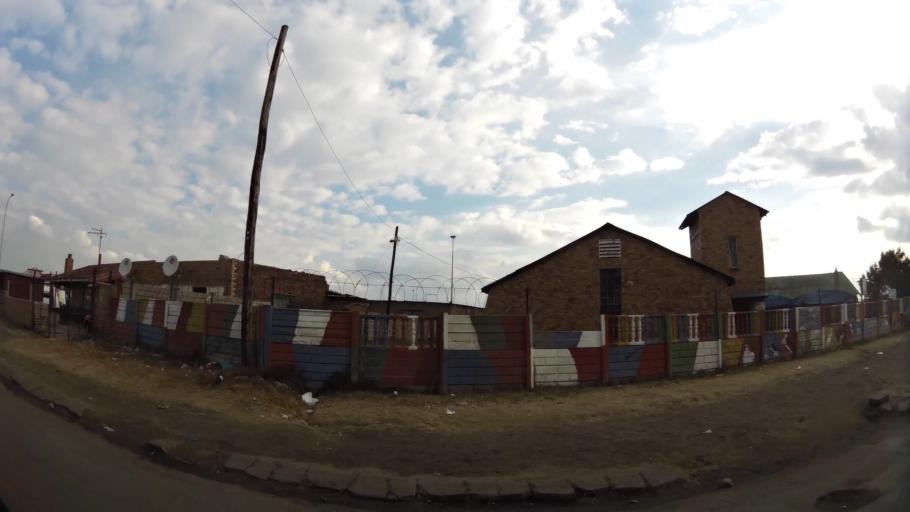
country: ZA
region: Gauteng
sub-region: Sedibeng District Municipality
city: Vanderbijlpark
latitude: -26.6967
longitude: 27.8738
